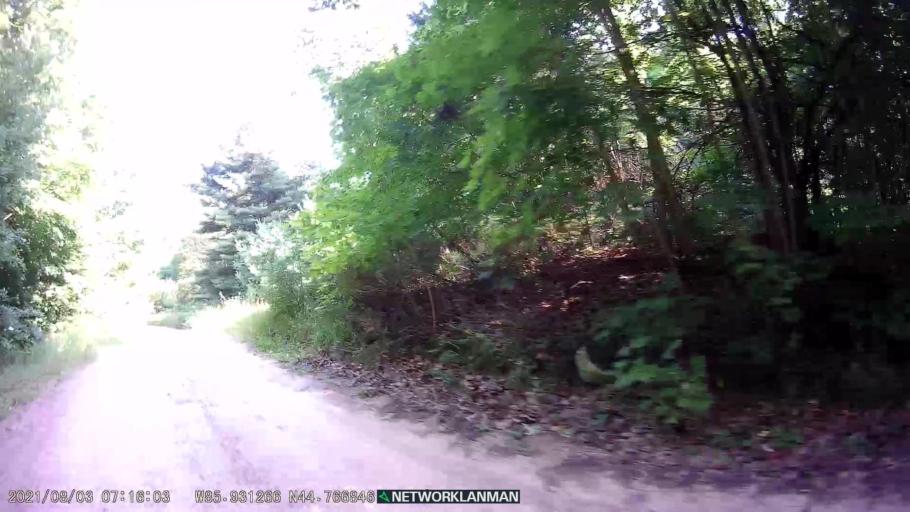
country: US
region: Michigan
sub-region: Benzie County
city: Beulah
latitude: 44.7669
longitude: -85.9315
